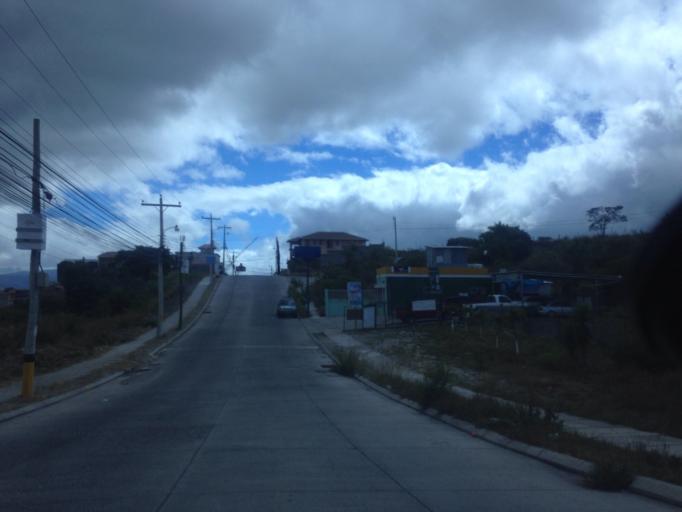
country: HN
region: Francisco Morazan
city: Yaguacire
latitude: 14.0518
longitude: -87.2422
